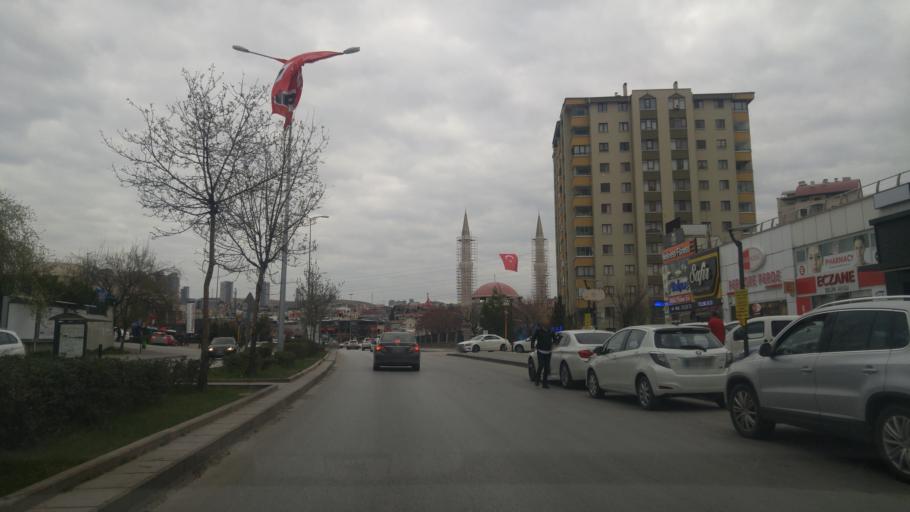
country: TR
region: Ankara
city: Etimesgut
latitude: 39.8753
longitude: 32.6873
